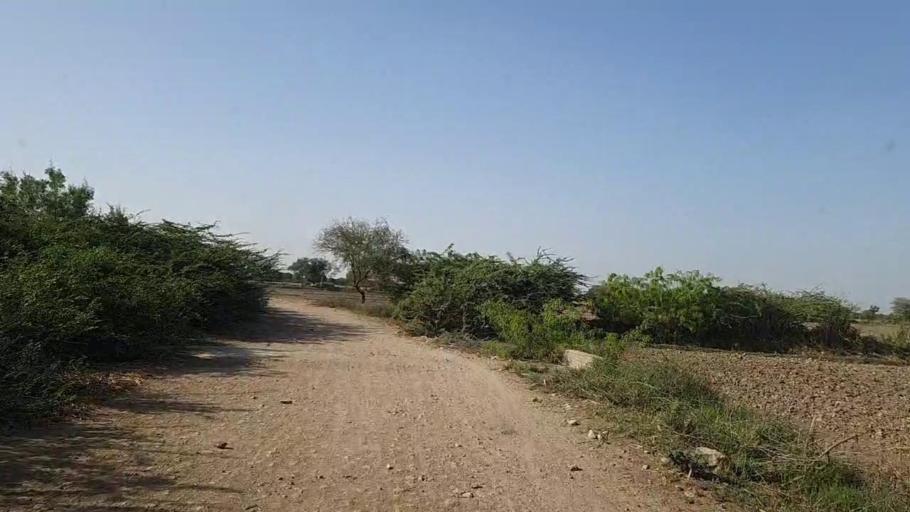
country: PK
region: Sindh
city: Kotri
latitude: 25.1408
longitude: 68.2792
